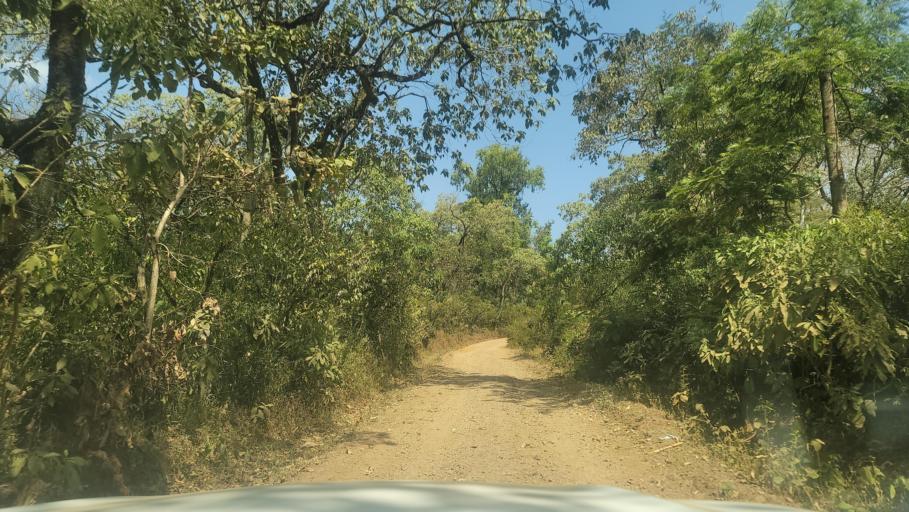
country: ET
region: Oromiya
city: Agaro
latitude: 7.8424
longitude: 36.5363
